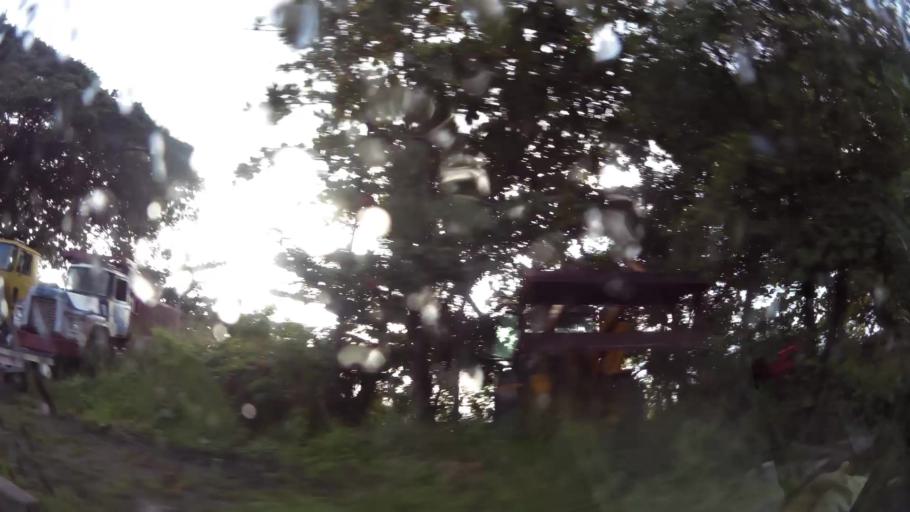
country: DM
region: Saint Paul
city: Mahaut
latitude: 15.3731
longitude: -61.4053
